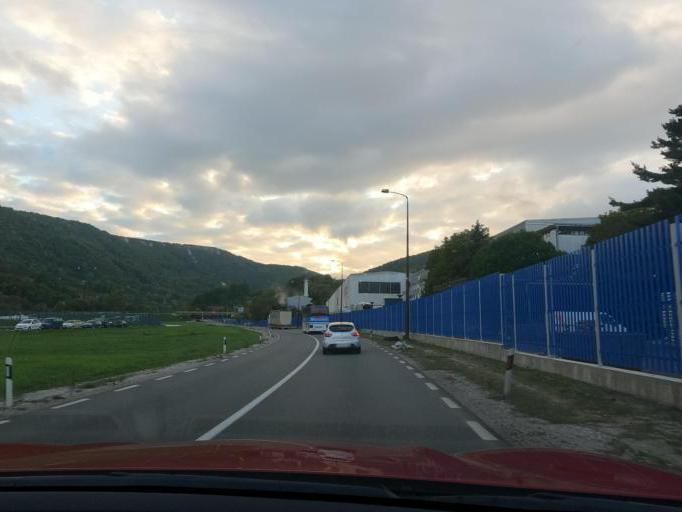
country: RS
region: Central Serbia
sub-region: Zlatiborski Okrug
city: Uzice
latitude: 43.8402
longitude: 19.8899
